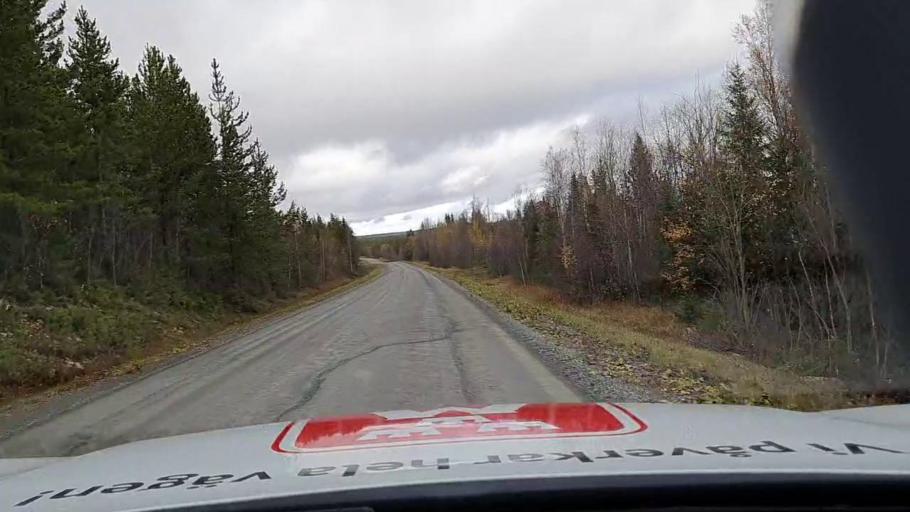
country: SE
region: Jaemtland
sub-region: Krokoms Kommun
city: Valla
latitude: 63.0559
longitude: 13.9633
